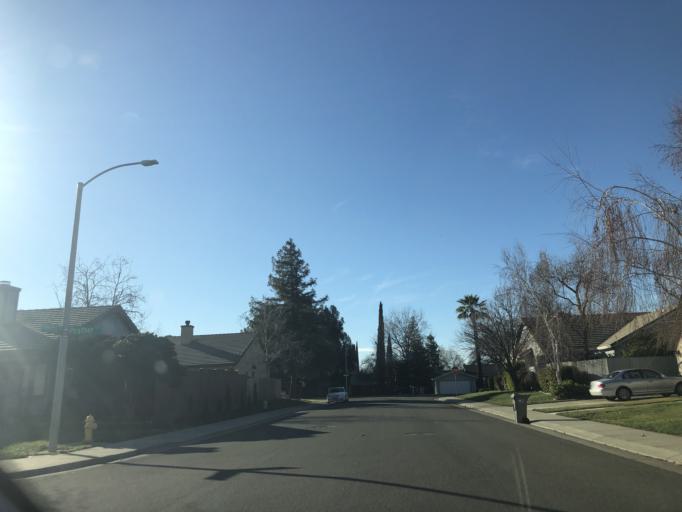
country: US
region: California
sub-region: Yolo County
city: Woodland
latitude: 38.6700
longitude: -121.7461
